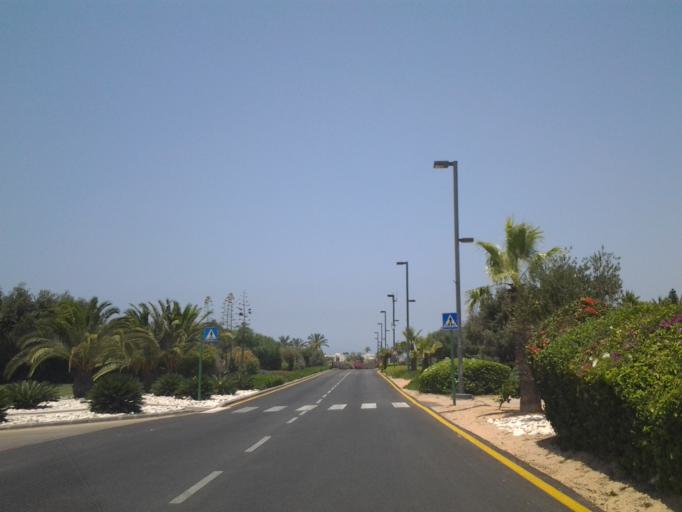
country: IL
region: Haifa
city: Qesarya
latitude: 32.5264
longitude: 34.9083
